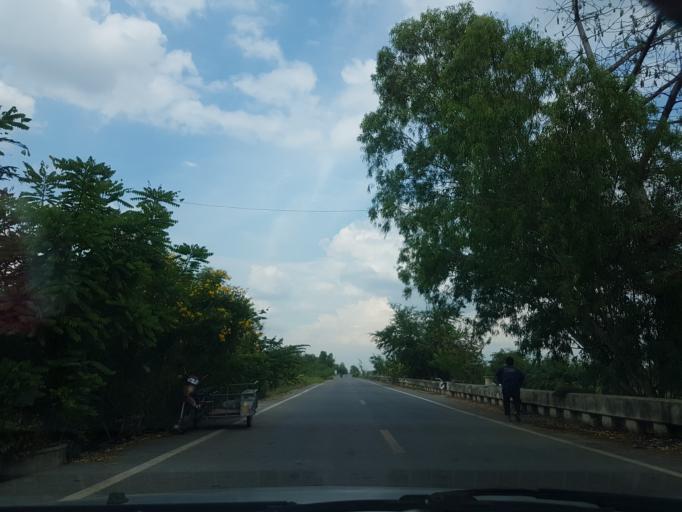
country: TH
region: Pathum Thani
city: Nong Suea
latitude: 14.1929
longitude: 100.8915
